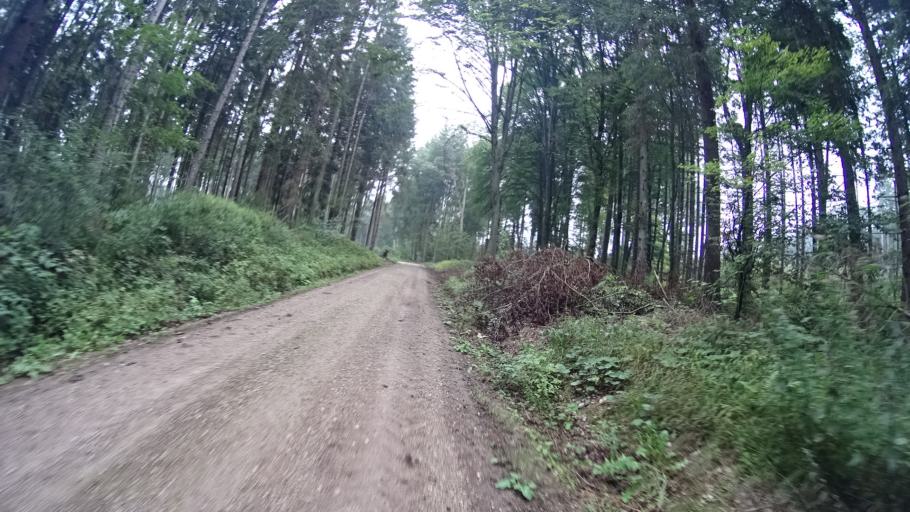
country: DE
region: Bavaria
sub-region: Upper Bavaria
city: Stammham
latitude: 48.8564
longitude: 11.4951
